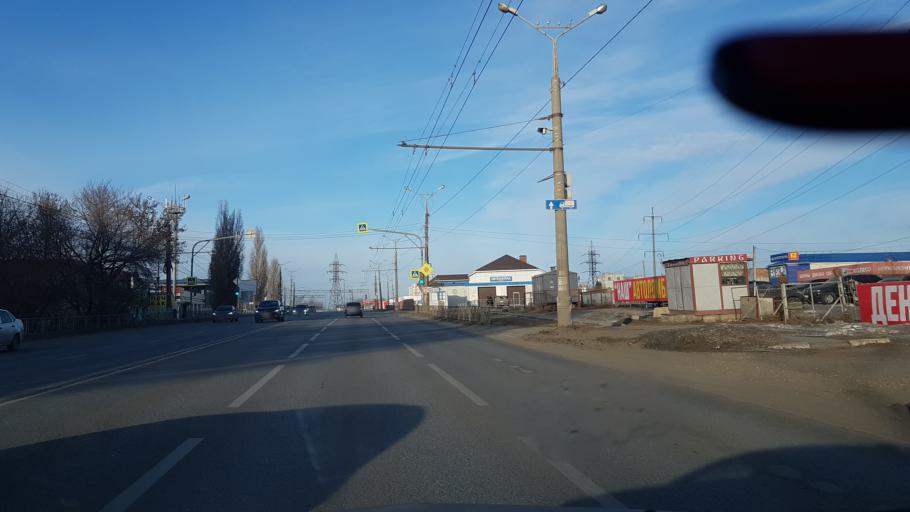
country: RU
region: Samara
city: Tol'yatti
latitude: 53.5329
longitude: 49.3960
